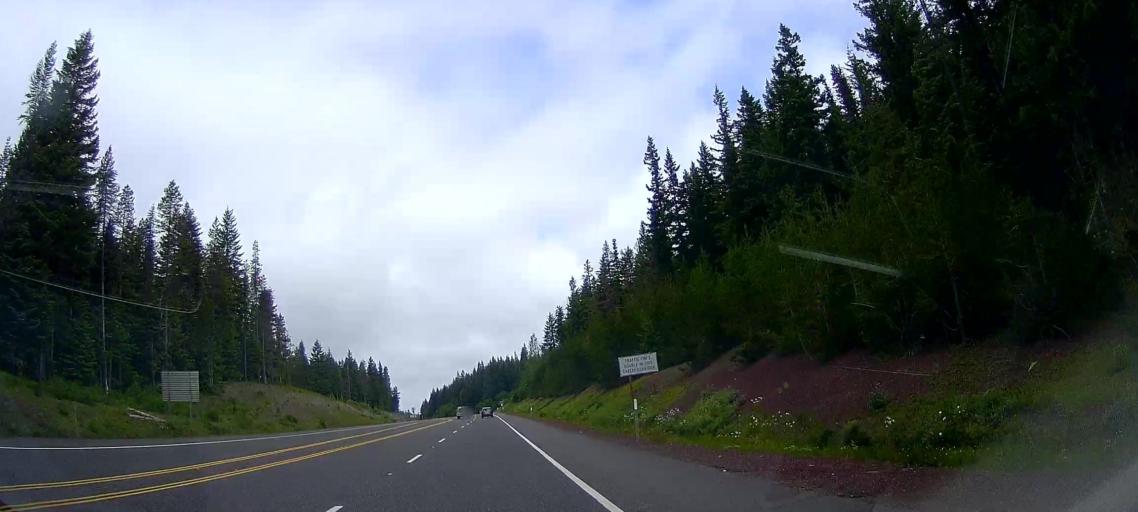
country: US
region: Oregon
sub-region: Clackamas County
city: Mount Hood Village
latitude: 45.2852
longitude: -121.7260
